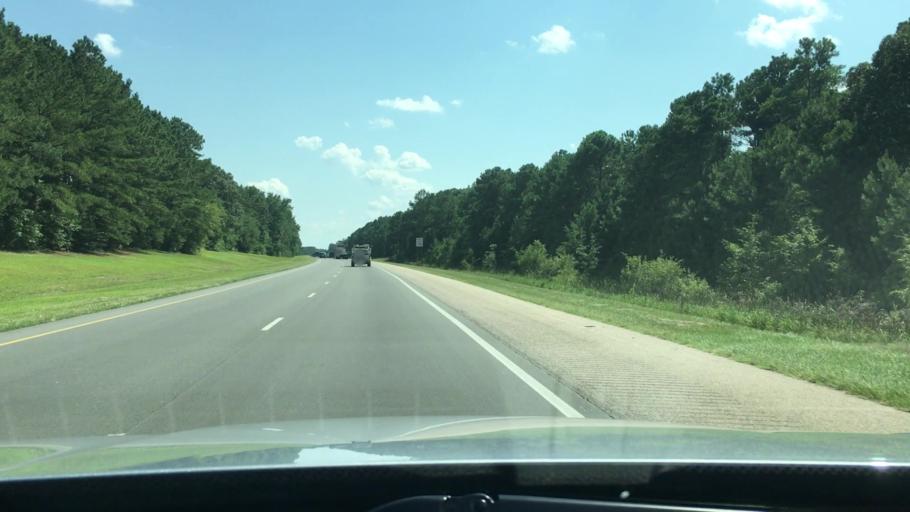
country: US
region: North Carolina
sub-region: Cumberland County
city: Eastover
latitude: 35.0737
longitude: -78.7916
